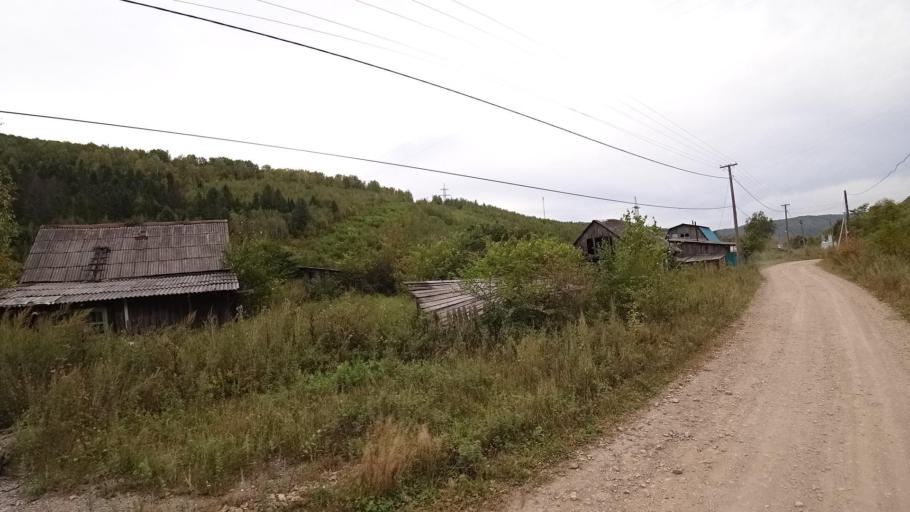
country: RU
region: Jewish Autonomous Oblast
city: Khingansk
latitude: 49.0265
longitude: 131.0743
